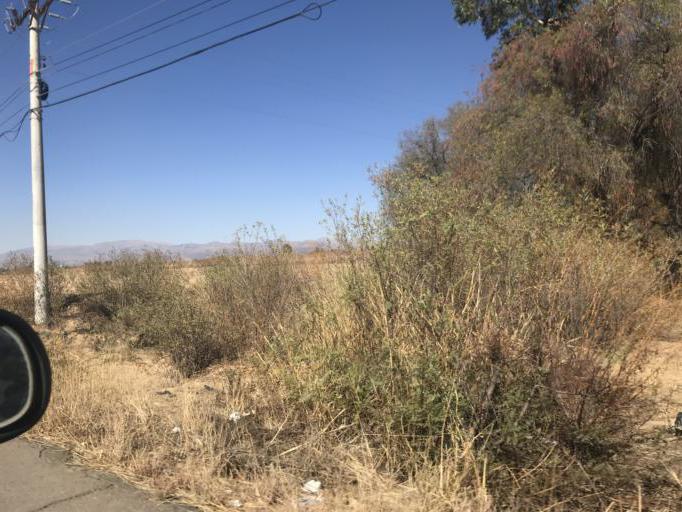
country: BO
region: Cochabamba
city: Tarata
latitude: -17.6041
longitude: -65.9904
